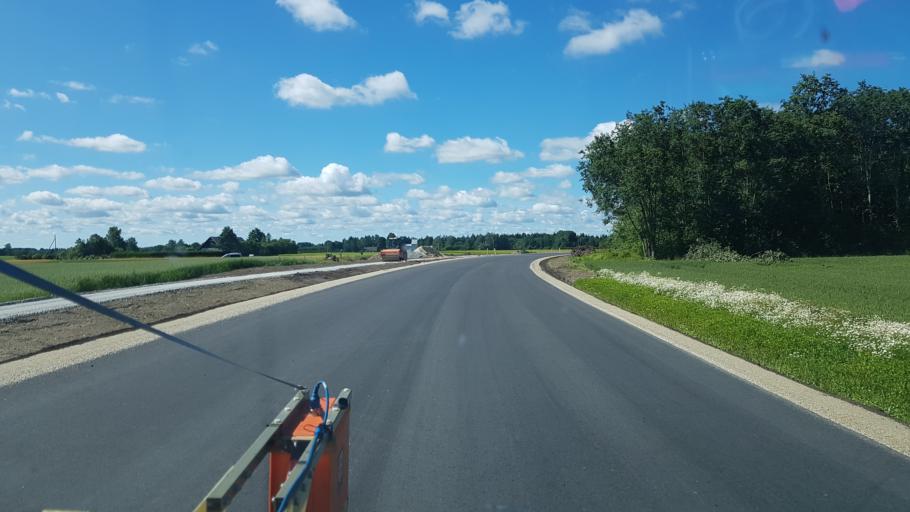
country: EE
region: Jaervamaa
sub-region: Paide linn
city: Paide
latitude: 58.8825
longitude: 25.7058
